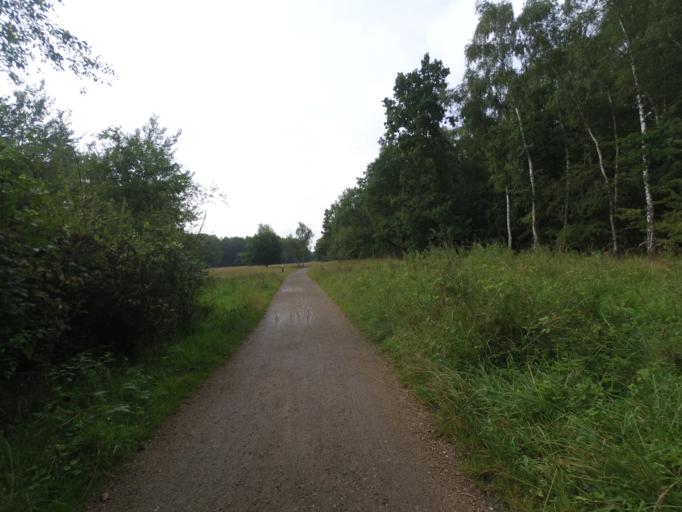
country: DE
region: Schleswig-Holstein
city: Oststeinbek
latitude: 53.5059
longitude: 10.1711
